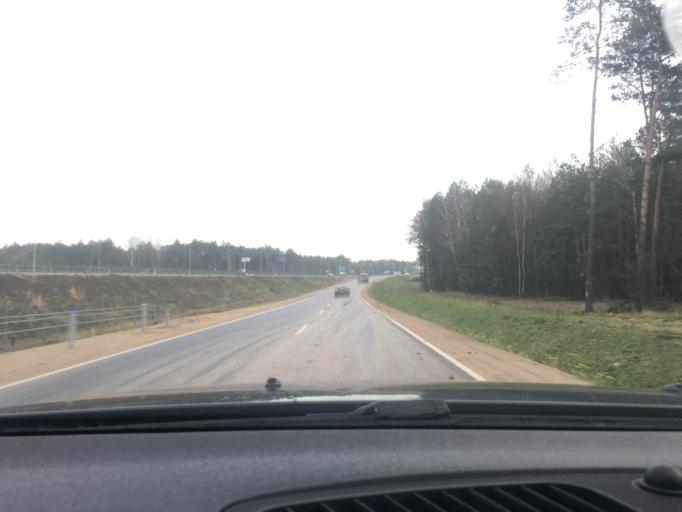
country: PL
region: Swietokrzyskie
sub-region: Powiat jedrzejowski
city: Jedrzejow
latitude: 50.6854
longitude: 20.3589
